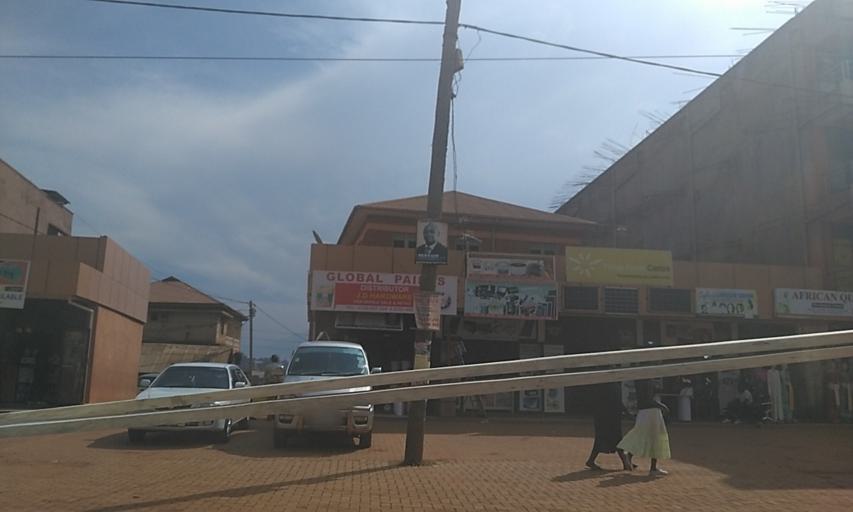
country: UG
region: Central Region
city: Kampala Central Division
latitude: 0.3012
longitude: 32.5287
